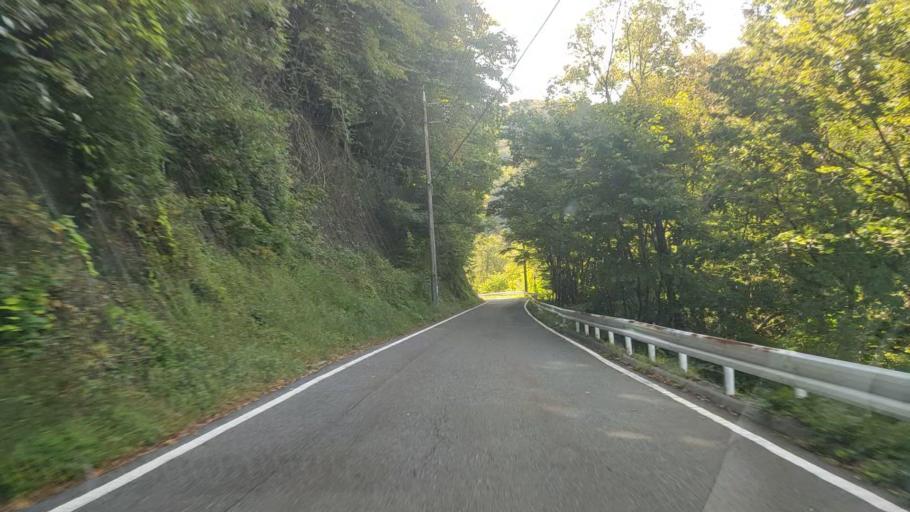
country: JP
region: Gunma
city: Nakanojomachi
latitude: 36.5972
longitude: 138.6914
